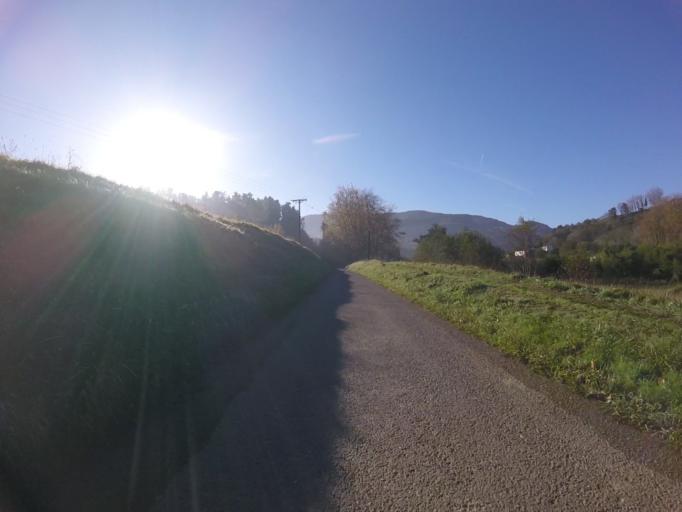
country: ES
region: Basque Country
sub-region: Provincia de Guipuzcoa
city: Usurbil
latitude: 43.2751
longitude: -2.0650
